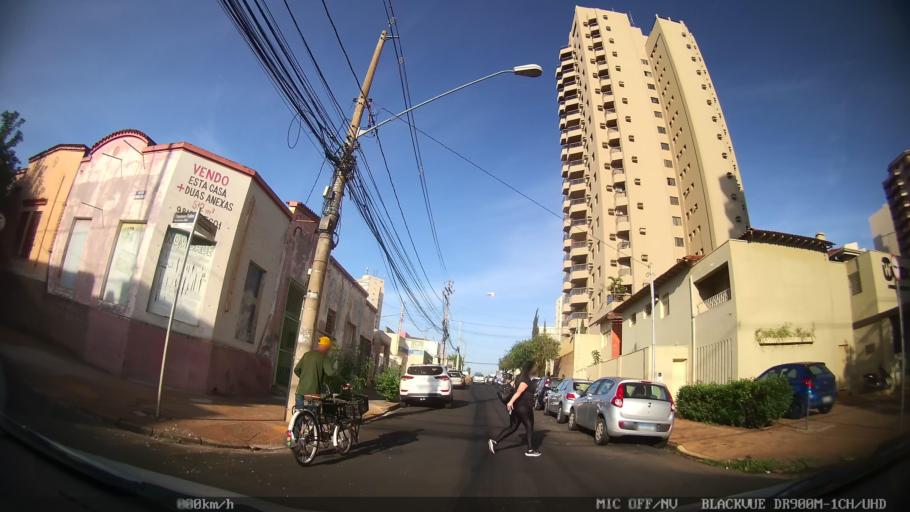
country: BR
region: Sao Paulo
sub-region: Ribeirao Preto
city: Ribeirao Preto
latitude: -21.1849
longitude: -47.8057
